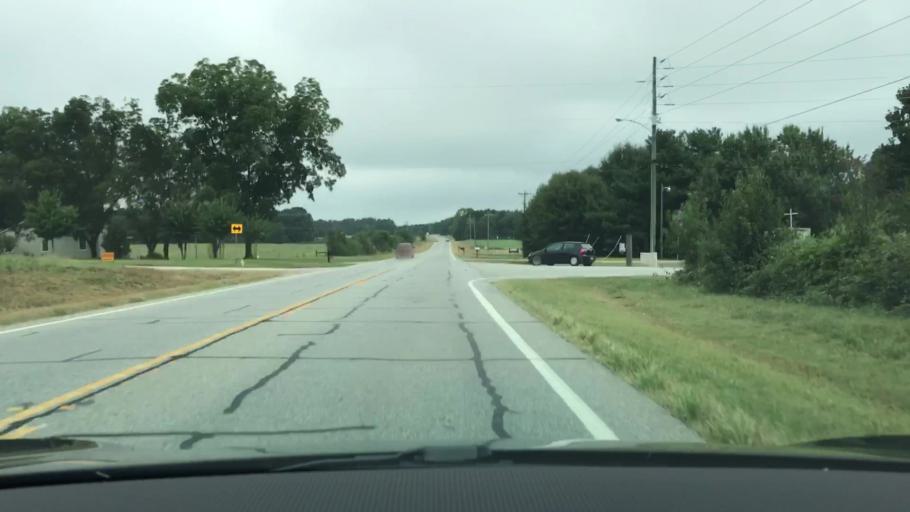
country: US
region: Georgia
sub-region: Oconee County
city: Watkinsville
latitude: 33.8374
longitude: -83.3836
